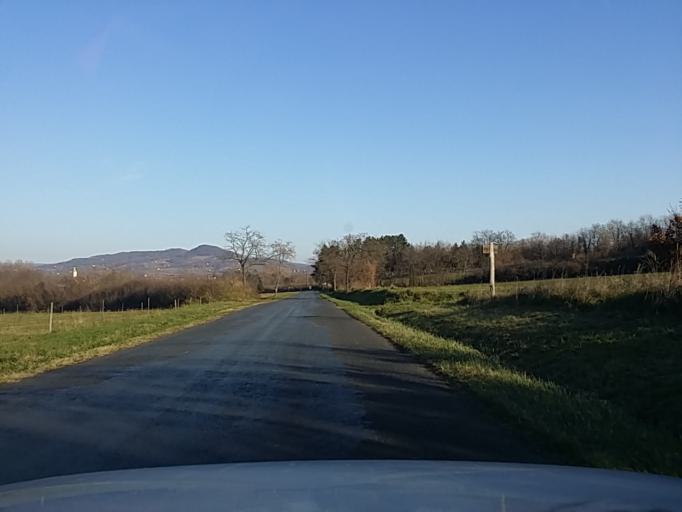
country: HU
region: Veszprem
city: Badacsonytomaj
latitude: 46.8414
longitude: 17.5131
